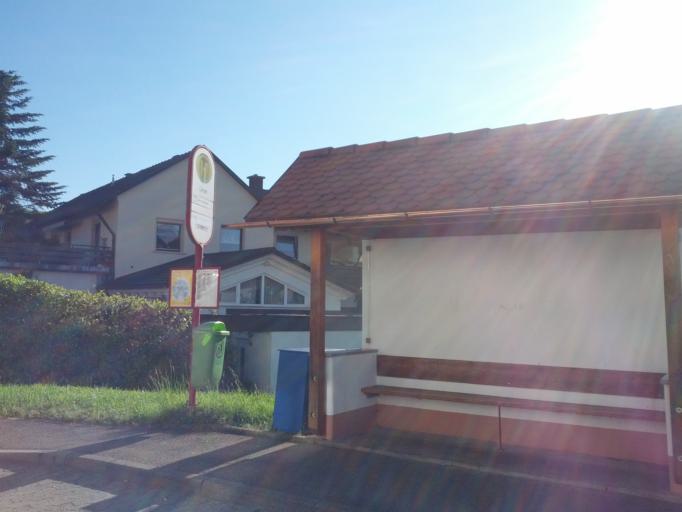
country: DE
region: Baden-Wuerttemberg
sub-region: Freiburg Region
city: Pfaffenweiler
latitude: 47.9362
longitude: 7.7588
